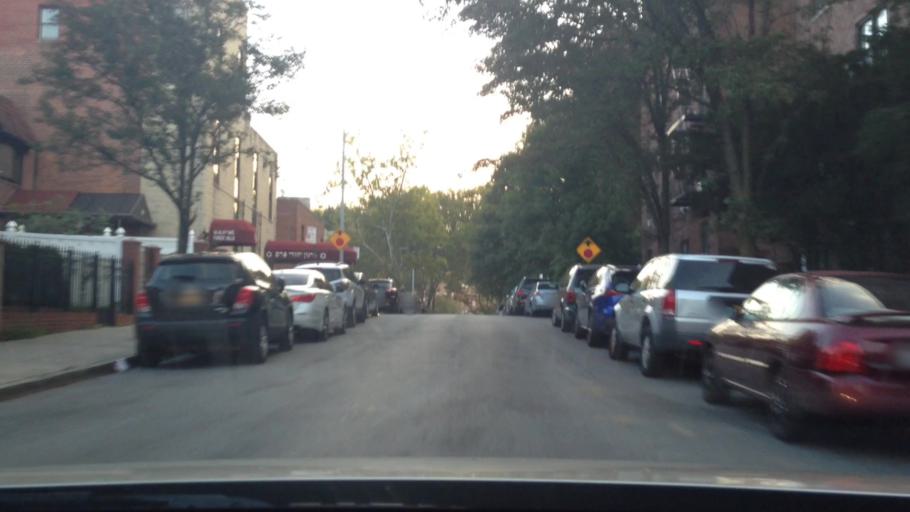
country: US
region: New York
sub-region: Queens County
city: Borough of Queens
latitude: 40.7249
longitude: -73.8551
